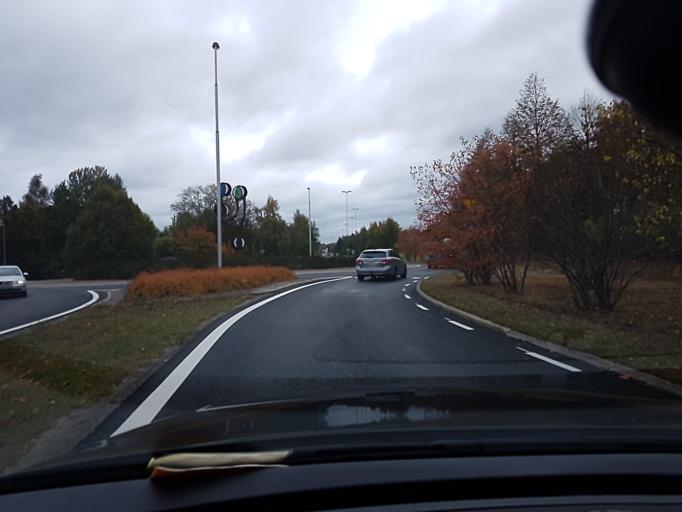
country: SE
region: Kronoberg
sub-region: Vaxjo Kommun
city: Vaexjoe
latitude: 56.8666
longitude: 14.8186
